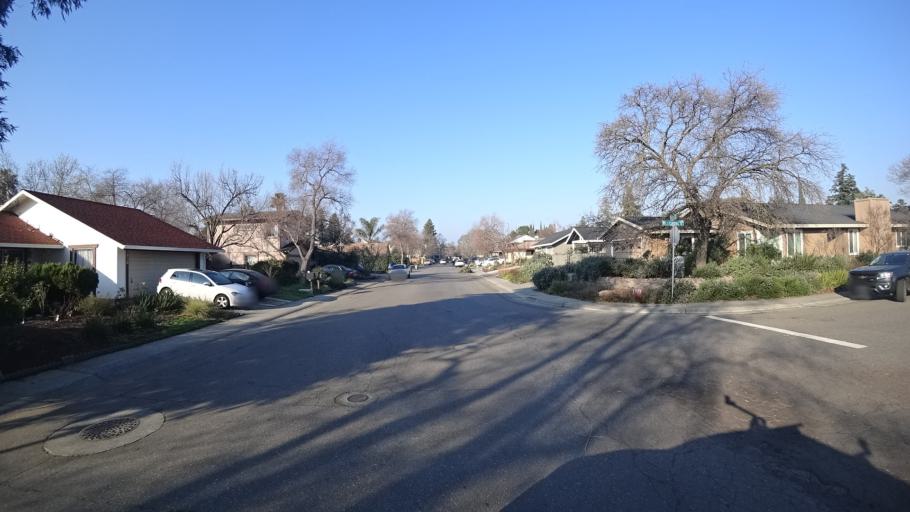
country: US
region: California
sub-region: Yolo County
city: Davis
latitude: 38.5564
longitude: -121.7850
